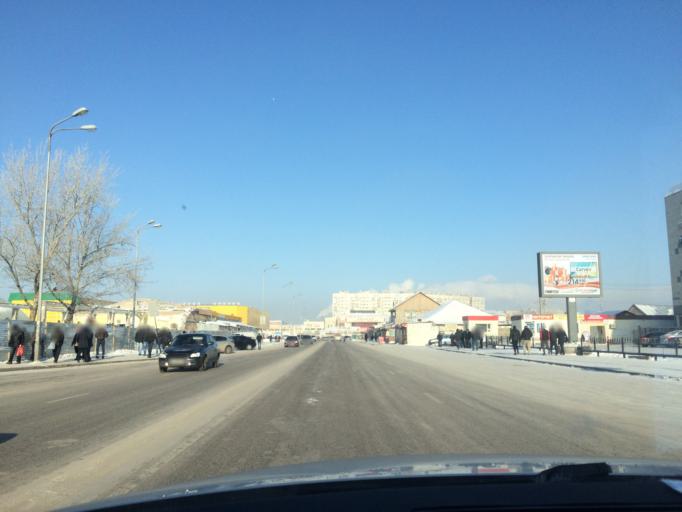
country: KZ
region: Astana Qalasy
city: Astana
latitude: 51.1758
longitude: 71.4374
